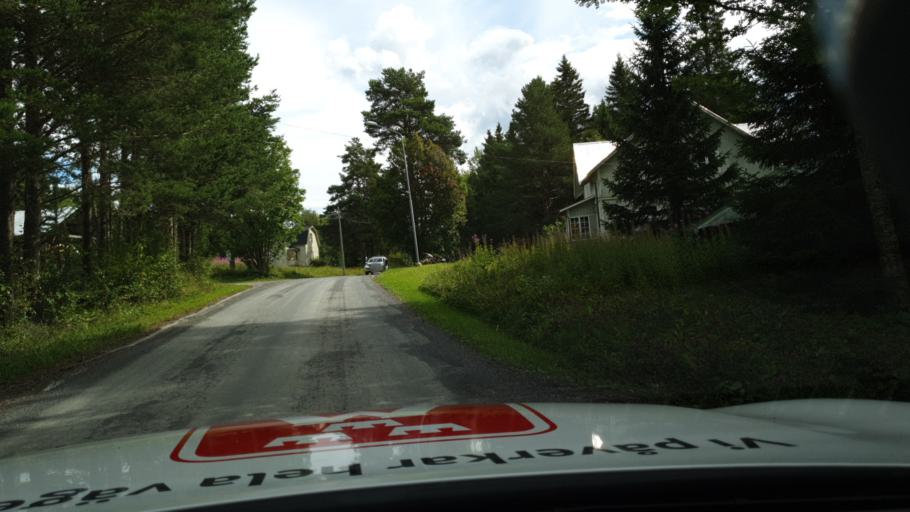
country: SE
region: Jaemtland
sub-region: Krokoms Kommun
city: Valla
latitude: 63.2687
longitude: 13.9520
